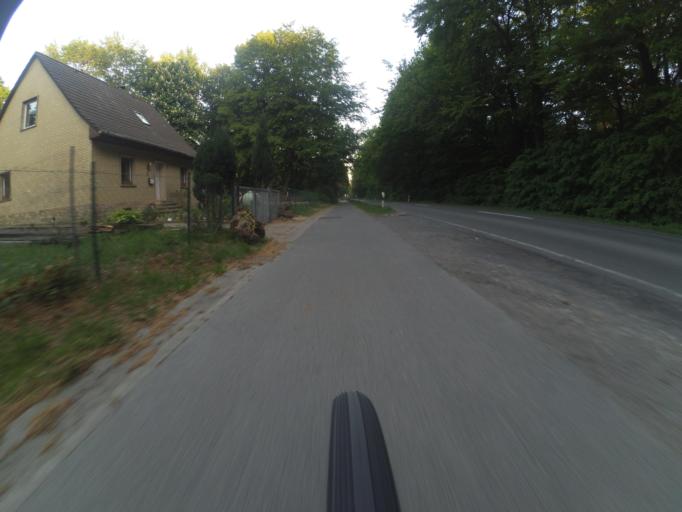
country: DE
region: North Rhine-Westphalia
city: Ibbenburen
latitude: 52.3112
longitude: 7.6792
